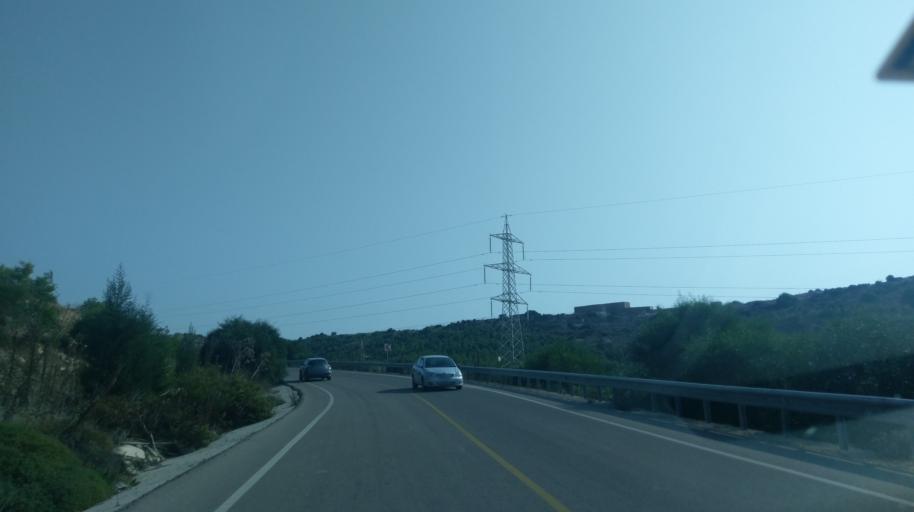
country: CY
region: Ammochostos
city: Leonarisso
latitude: 35.4769
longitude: 34.1359
